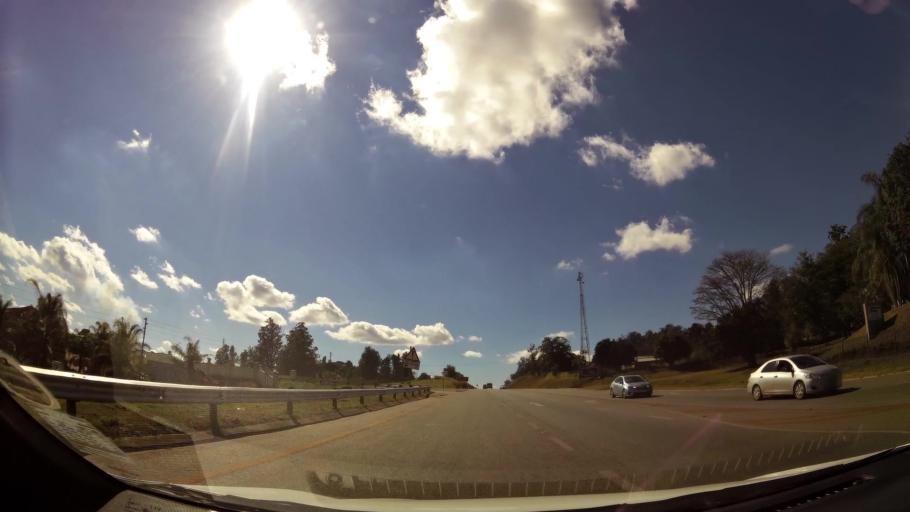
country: ZA
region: Limpopo
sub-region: Mopani District Municipality
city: Tzaneen
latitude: -23.8176
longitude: 30.1690
